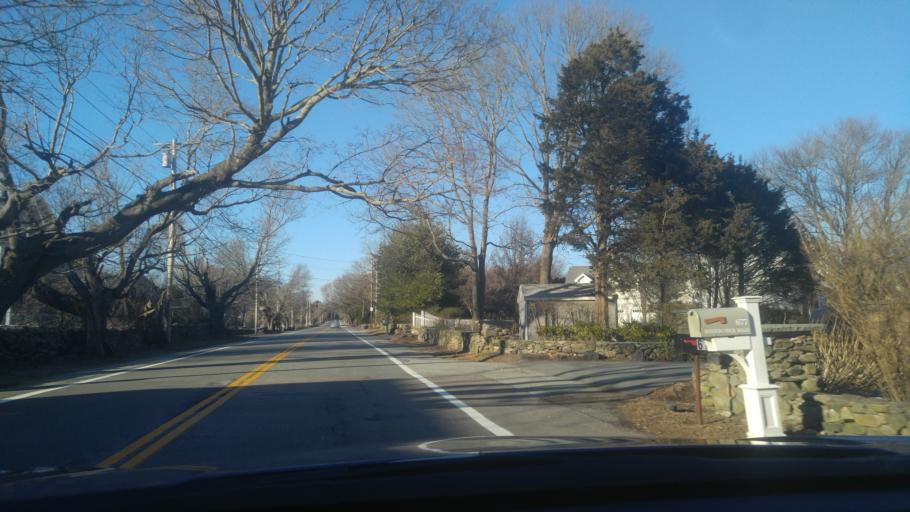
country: US
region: Rhode Island
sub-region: Washington County
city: Narragansett Pier
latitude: 41.4636
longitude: -71.4328
